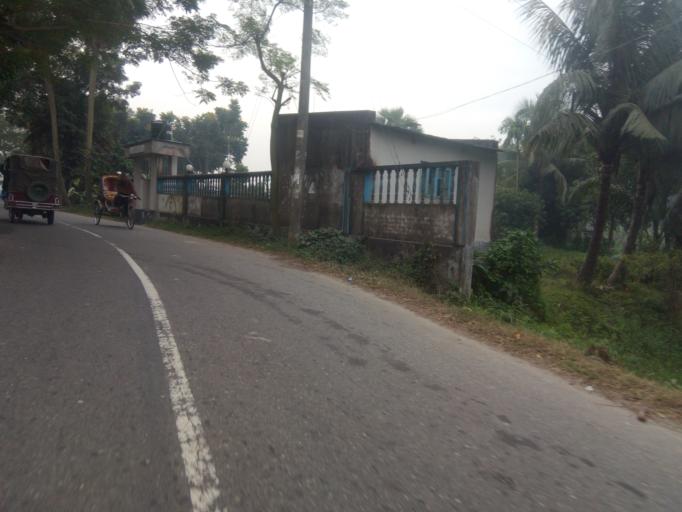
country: BD
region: Dhaka
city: Narayanganj
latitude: 23.5356
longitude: 90.4849
